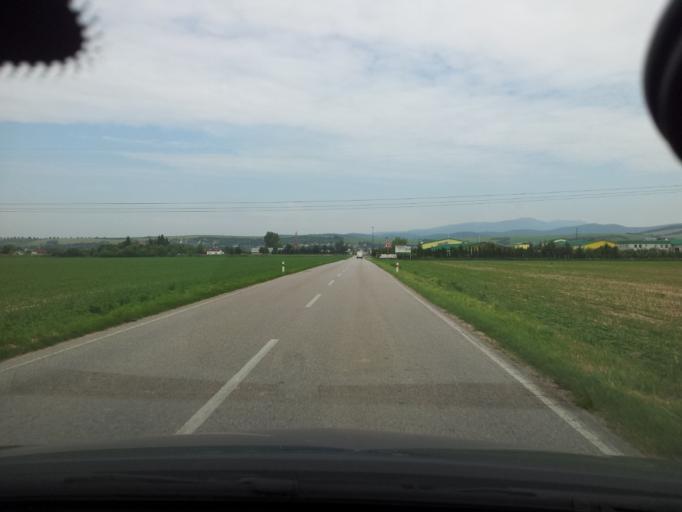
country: SK
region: Nitriansky
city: Partizanske
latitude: 48.6211
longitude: 18.4294
